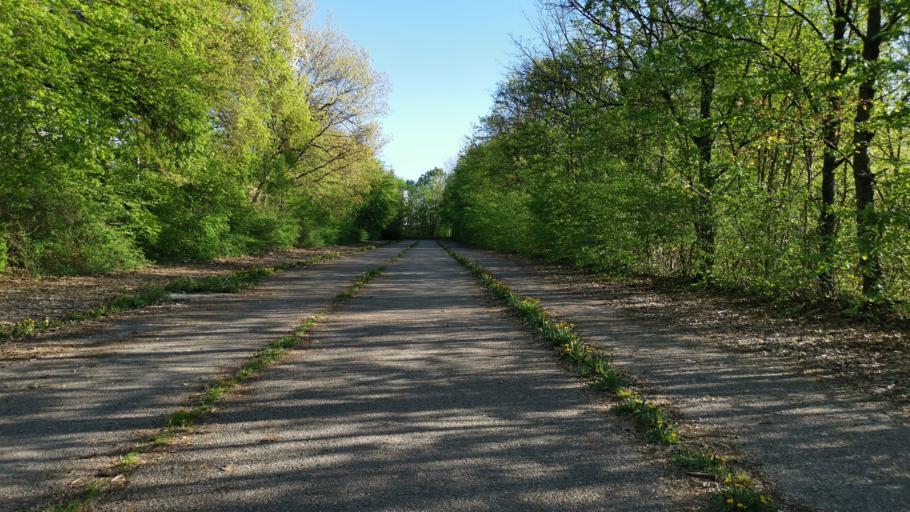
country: DE
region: Bavaria
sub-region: Upper Bavaria
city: Pullach im Isartal
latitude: 48.0892
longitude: 11.5303
